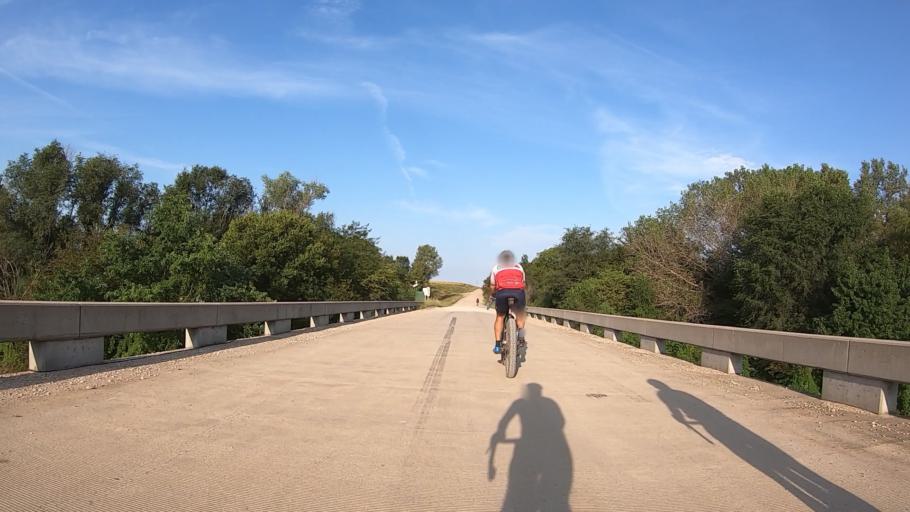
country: US
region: Kansas
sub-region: Marshall County
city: Blue Rapids
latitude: 39.7258
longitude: -96.8047
